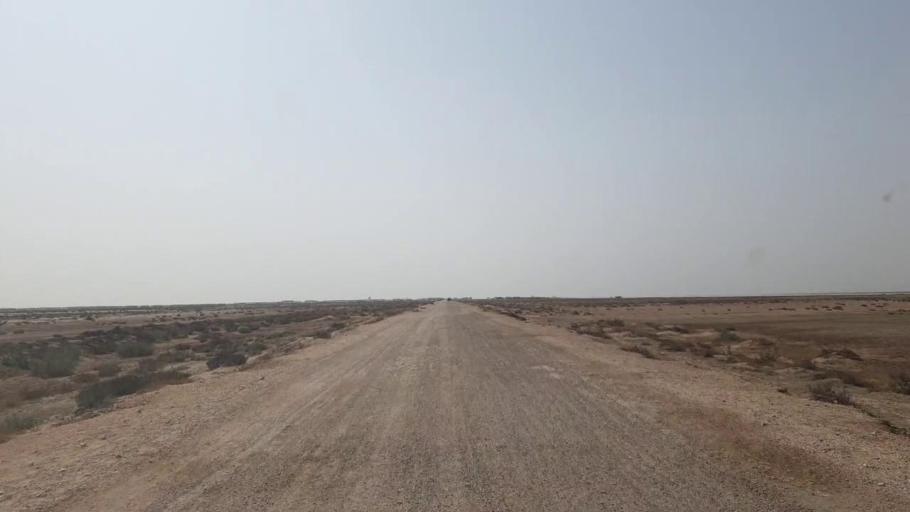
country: PK
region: Sindh
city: Jati
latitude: 24.3516
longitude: 68.5937
